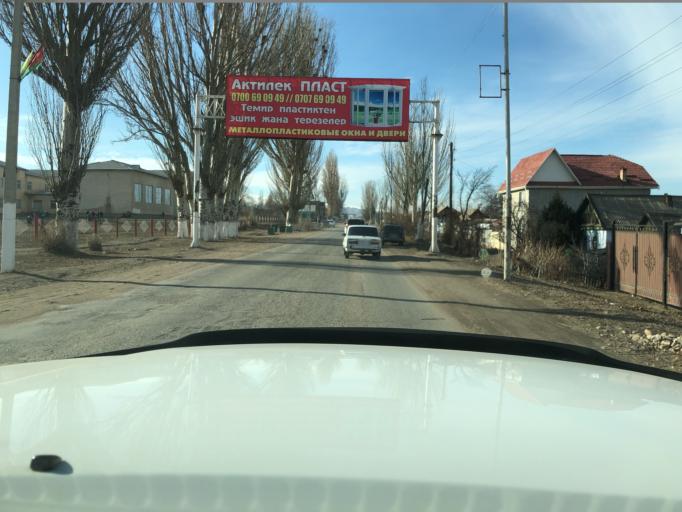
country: KG
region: Ysyk-Koel
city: Pokrovka
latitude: 42.3362
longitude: 77.9918
